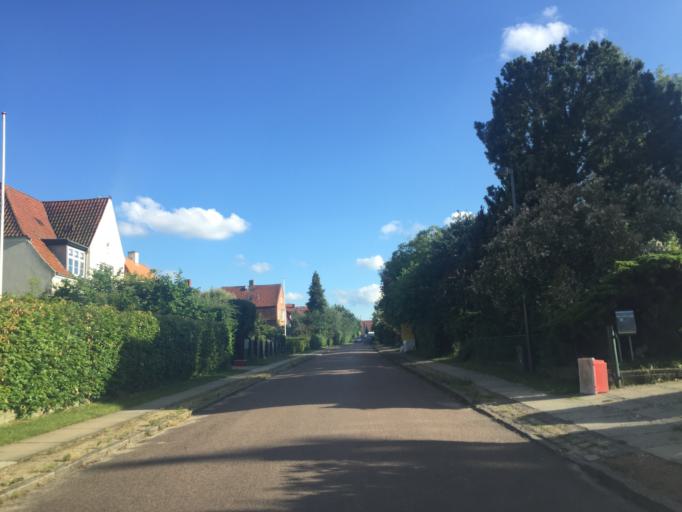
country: DK
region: Capital Region
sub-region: Kobenhavn
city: Vanlose
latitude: 55.7090
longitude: 12.4962
